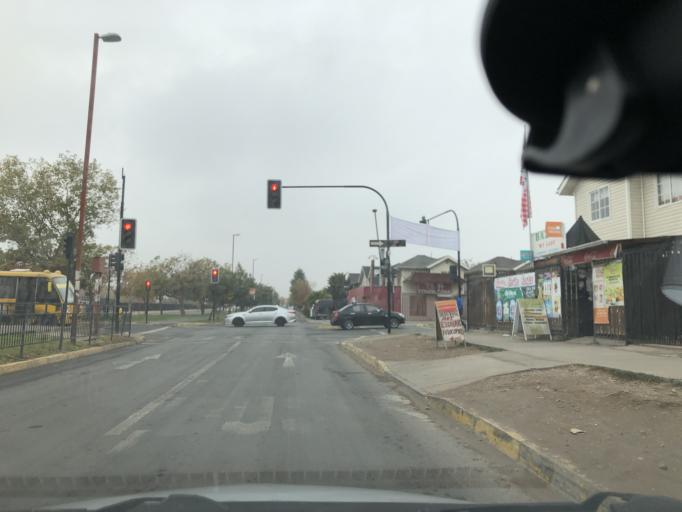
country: CL
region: Santiago Metropolitan
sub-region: Provincia de Cordillera
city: Puente Alto
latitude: -33.5960
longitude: -70.5850
